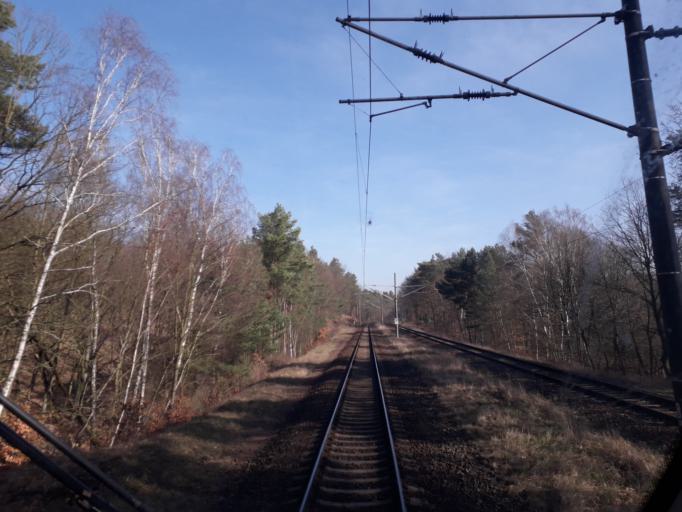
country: DE
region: Brandenburg
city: Michendorf
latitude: 52.3076
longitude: 12.9657
